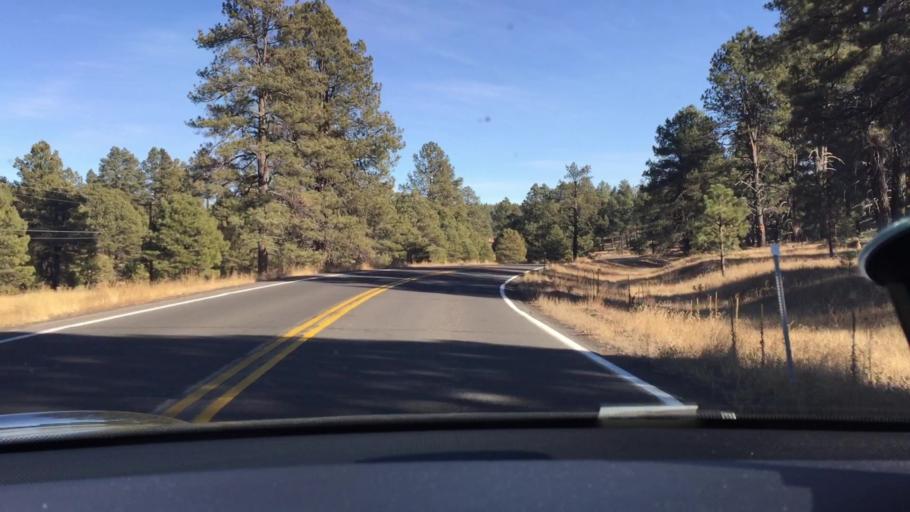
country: US
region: Arizona
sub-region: Coconino County
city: Mountainaire
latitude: 35.0927
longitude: -111.6759
